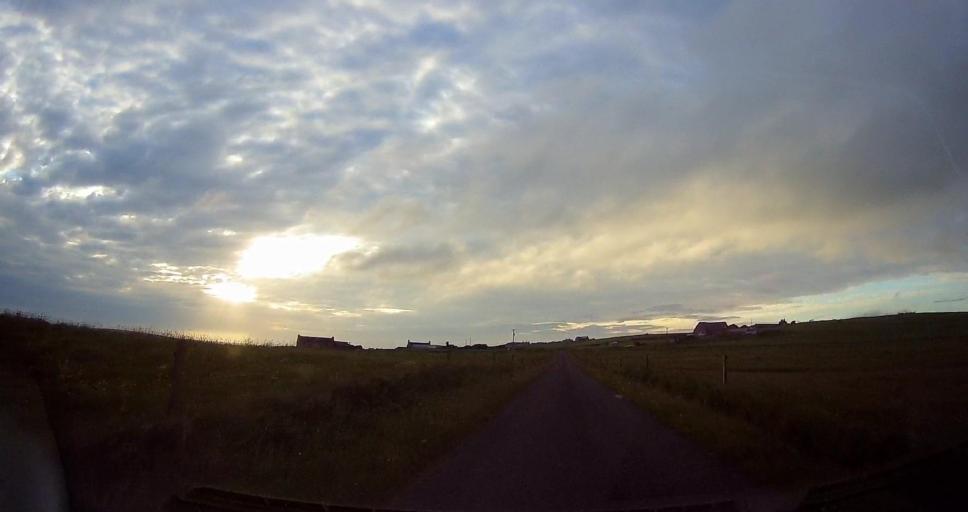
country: GB
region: Scotland
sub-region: Orkney Islands
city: Stromness
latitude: 59.1225
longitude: -3.2776
